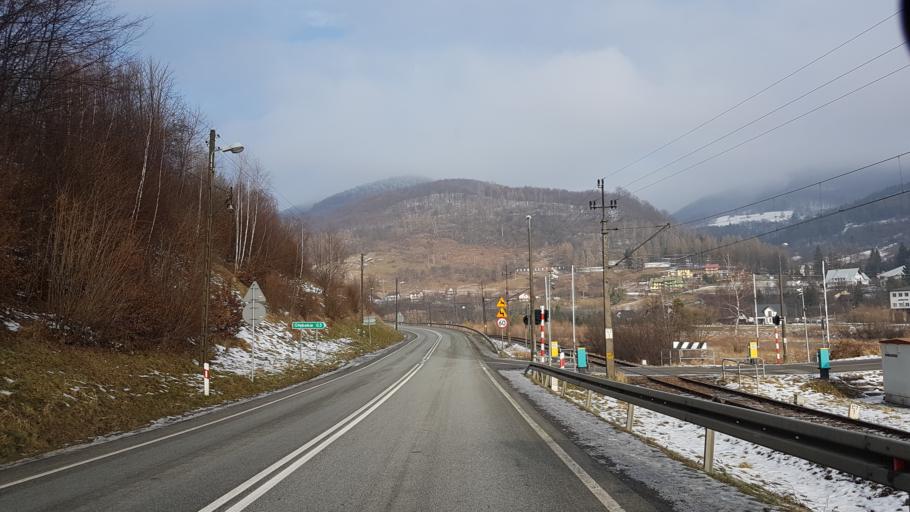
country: PL
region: Lesser Poland Voivodeship
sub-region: Powiat nowosadecki
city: Piwniczna-Zdroj
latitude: 49.4650
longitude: 20.6972
